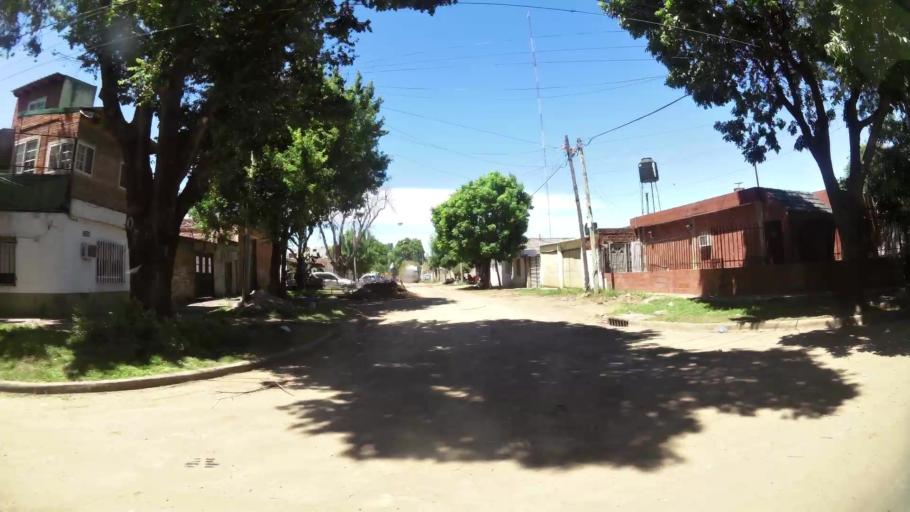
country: AR
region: Santa Fe
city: Perez
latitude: -32.9488
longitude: -60.7146
